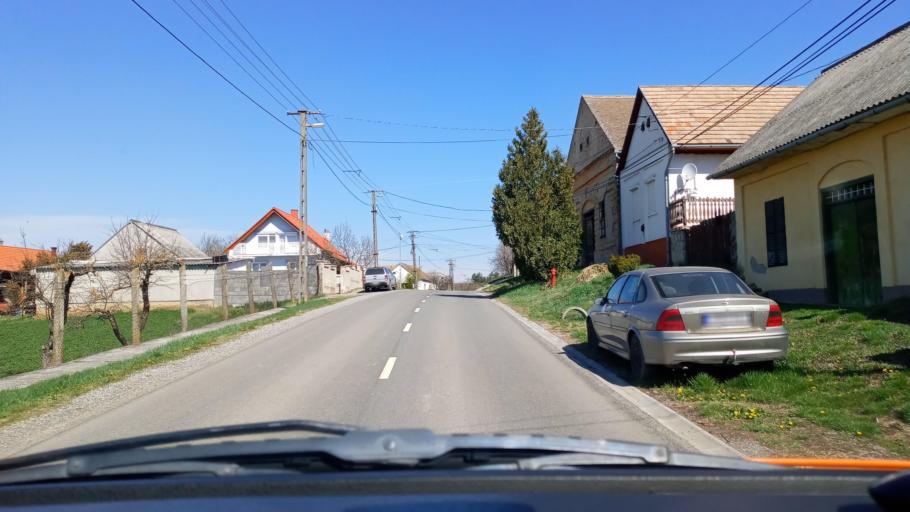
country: HU
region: Baranya
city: Boly
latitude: 45.9995
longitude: 18.4593
